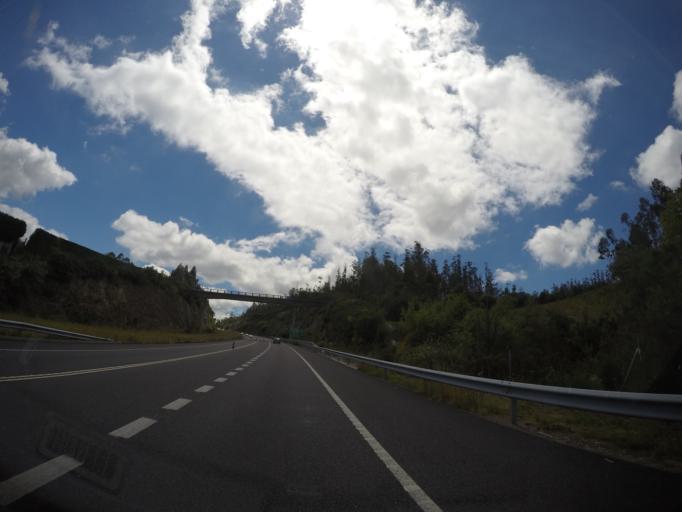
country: ES
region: Aragon
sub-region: Provincia de Zaragoza
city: El Burgo de Ebro
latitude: 41.5551
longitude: -0.7609
